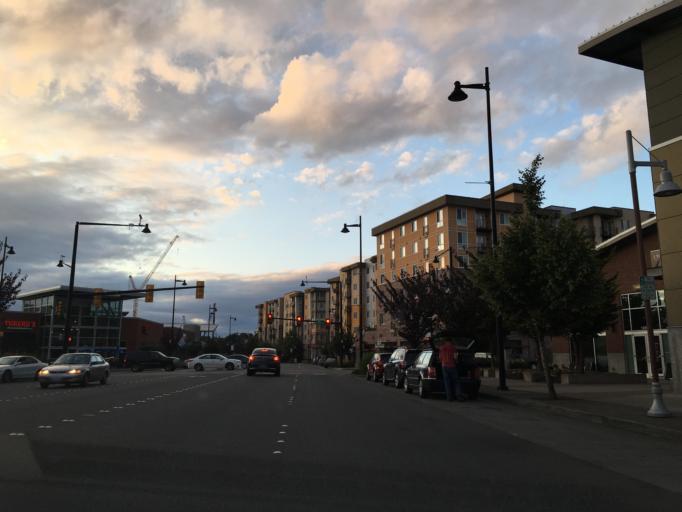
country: US
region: Washington
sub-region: King County
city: Renton
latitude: 47.4974
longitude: -122.2021
